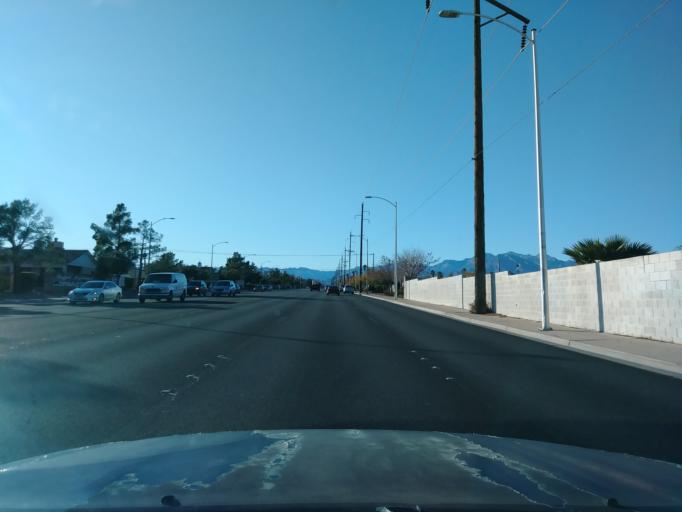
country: US
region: Nevada
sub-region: Clark County
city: Spring Valley
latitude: 36.1592
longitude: -115.2571
